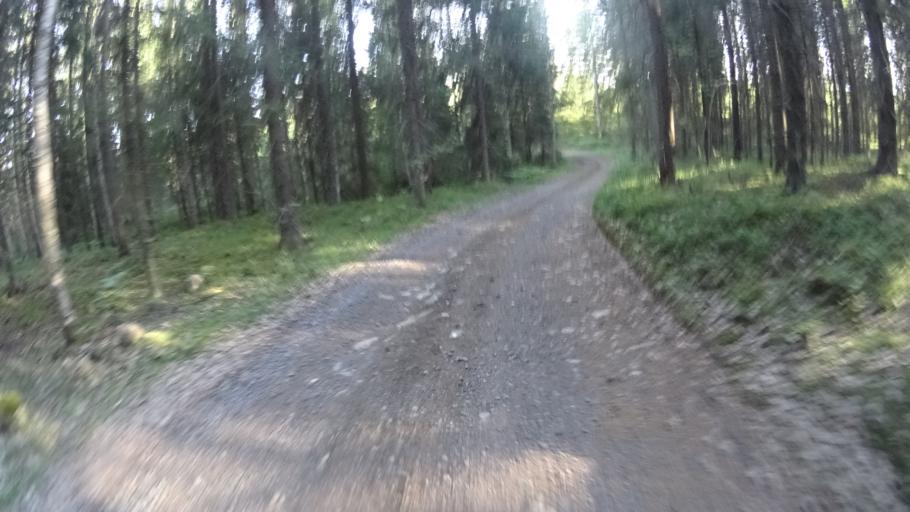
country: FI
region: Uusimaa
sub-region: Helsinki
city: Karkkila
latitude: 60.5967
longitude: 24.1090
